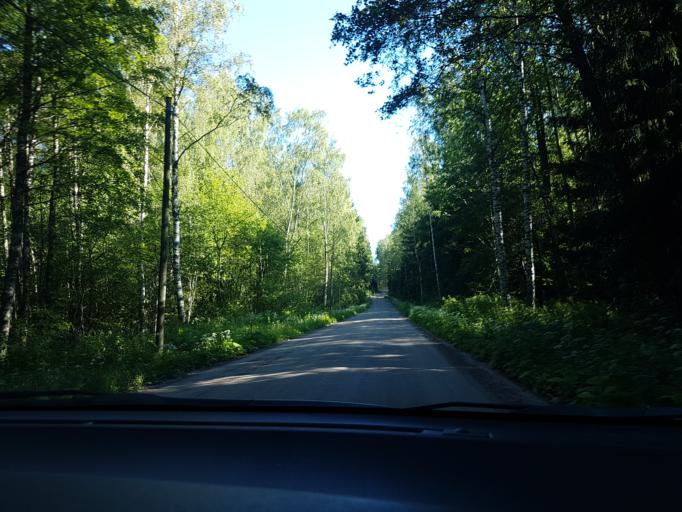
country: FI
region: Uusimaa
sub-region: Helsinki
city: Sibbo
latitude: 60.2674
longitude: 25.2287
